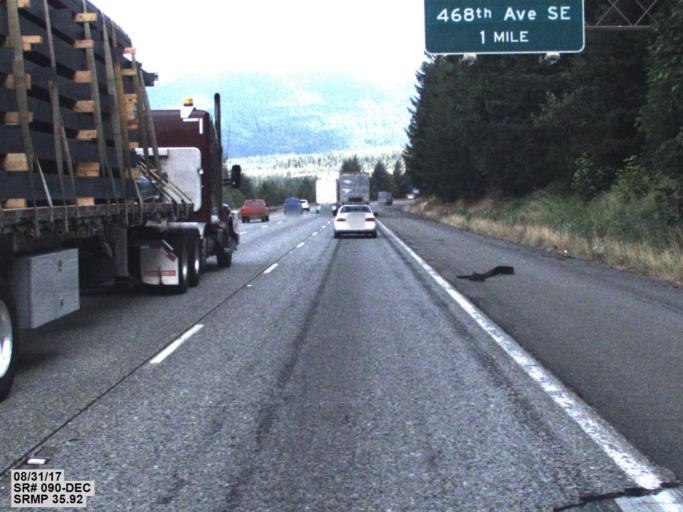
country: US
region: Washington
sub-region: King County
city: Tanner
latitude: 47.4526
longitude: -121.7007
